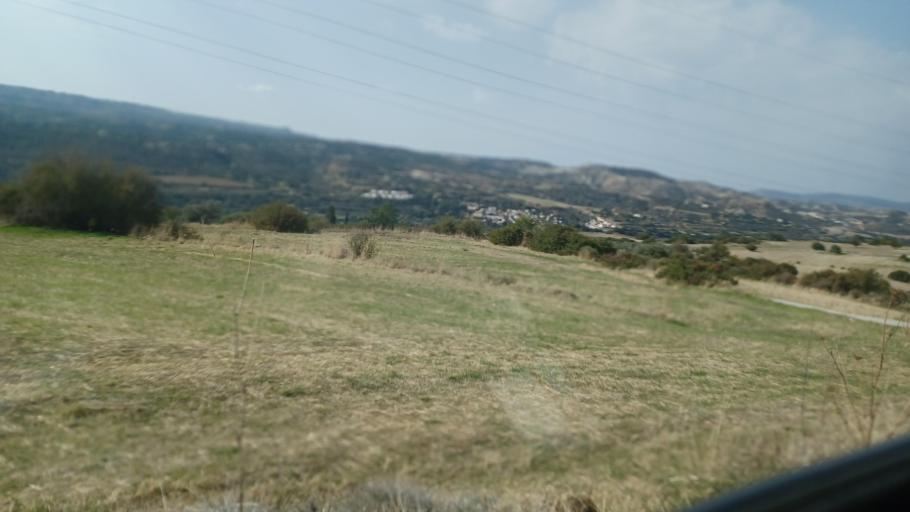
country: CY
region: Pafos
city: Polis
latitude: 34.9921
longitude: 32.4558
